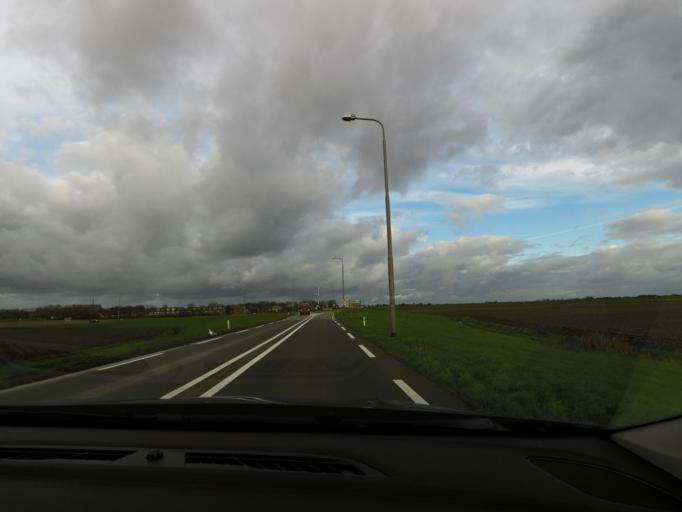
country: NL
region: Zeeland
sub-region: Schouwen-Duiveland
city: Scharendijke
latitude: 51.7186
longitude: 3.9046
